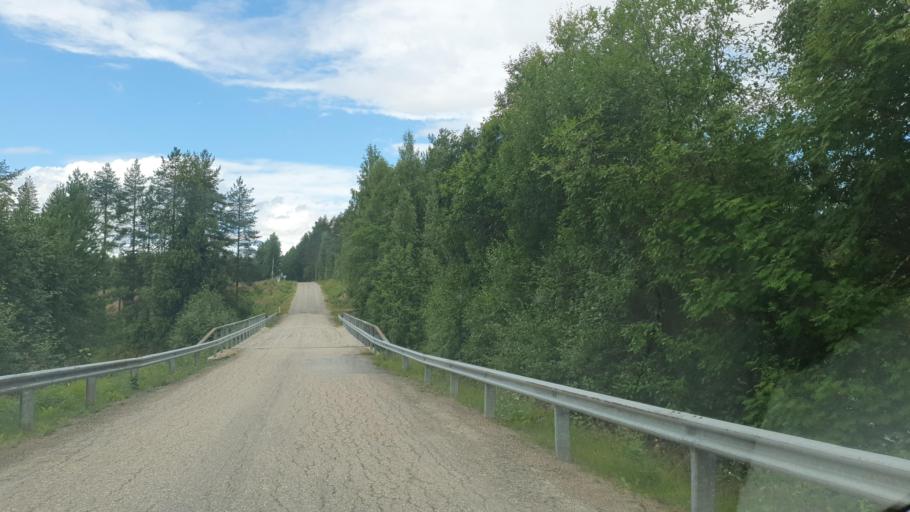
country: FI
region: Kainuu
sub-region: Kehys-Kainuu
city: Kuhmo
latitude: 64.1084
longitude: 29.3866
